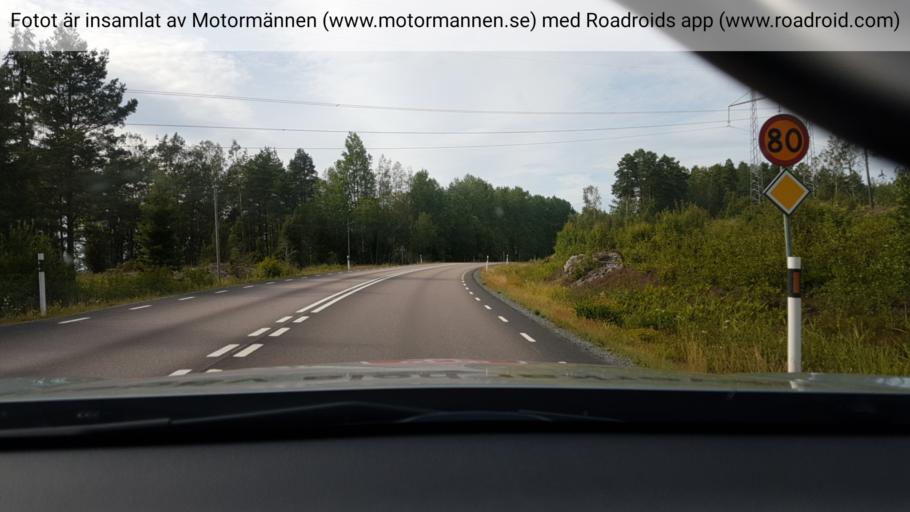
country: SE
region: Vaestra Goetaland
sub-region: Amals Kommun
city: Amal
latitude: 59.0587
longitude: 12.6551
